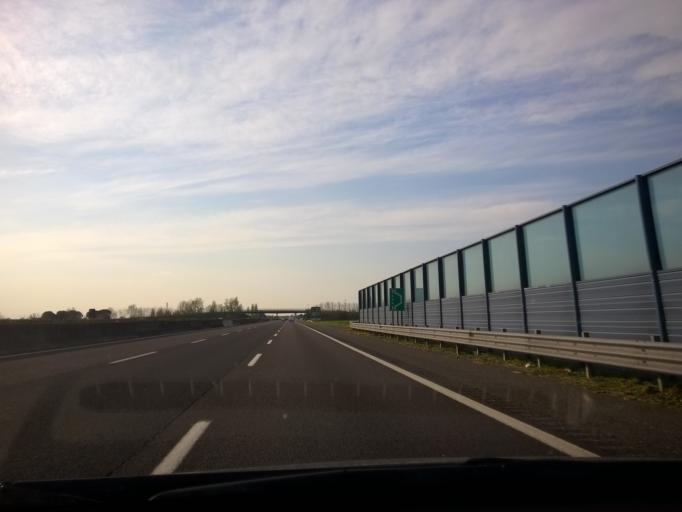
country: IT
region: Emilia-Romagna
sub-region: Forli-Cesena
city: Santa Maria Nuova
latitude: 44.2122
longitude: 12.1853
